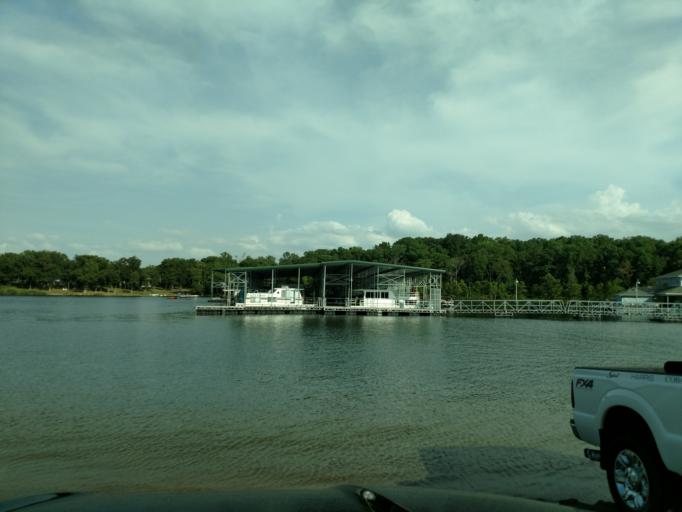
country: US
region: Missouri
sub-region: Barry County
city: Shell Knob
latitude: 36.5958
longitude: -93.5488
